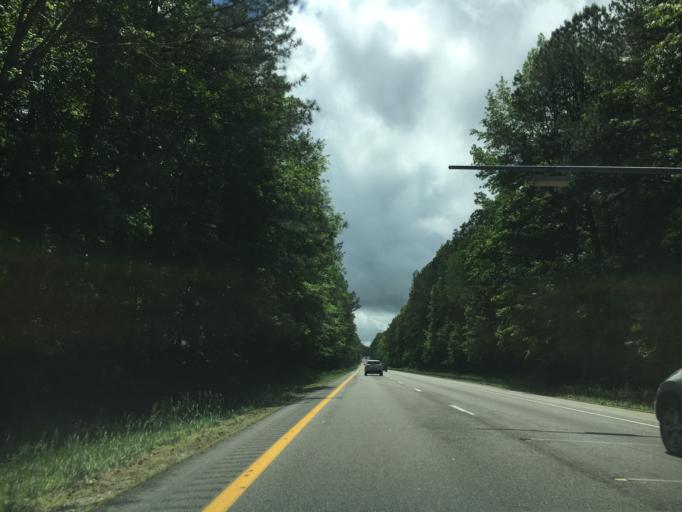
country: US
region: Virginia
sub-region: Brunswick County
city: Lawrenceville
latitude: 36.8125
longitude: -77.9744
